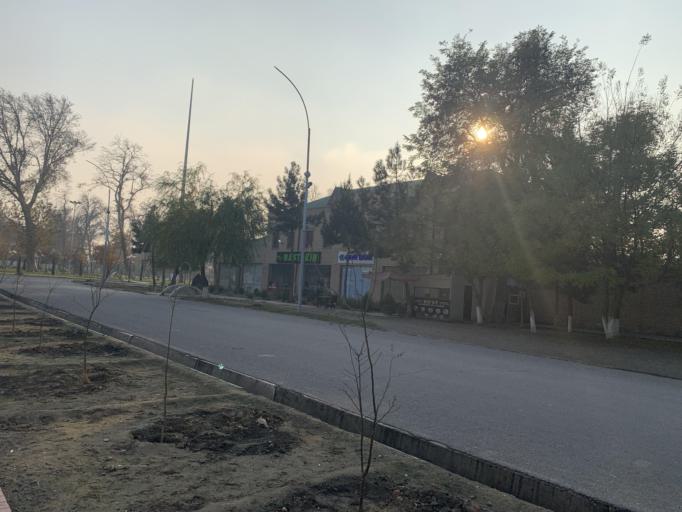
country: UZ
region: Fergana
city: Qo`qon
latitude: 40.5385
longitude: 70.9354
